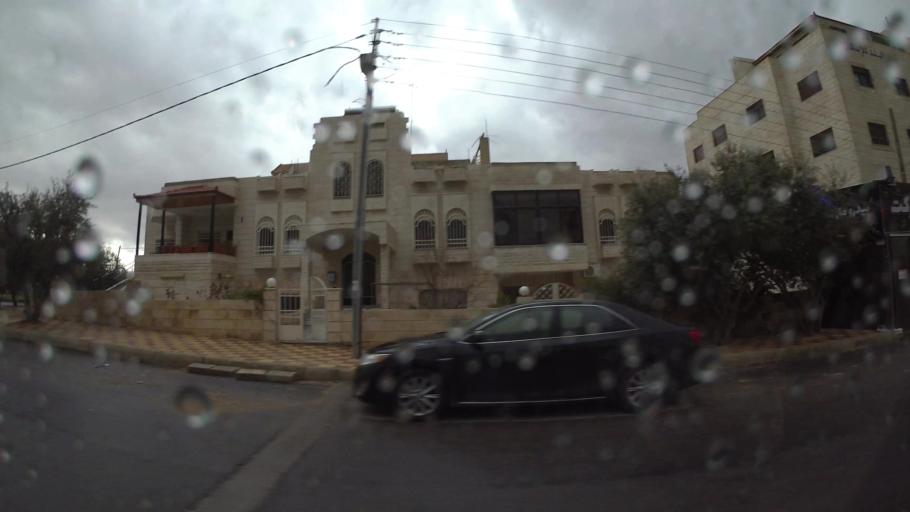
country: JO
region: Amman
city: Amman
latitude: 32.0066
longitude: 35.9560
